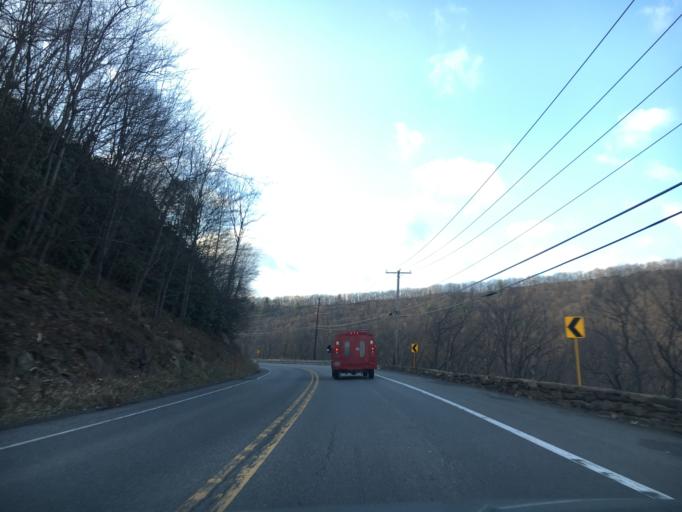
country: US
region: Pennsylvania
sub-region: Carbon County
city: Jim Thorpe
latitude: 40.8623
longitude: -75.7208
